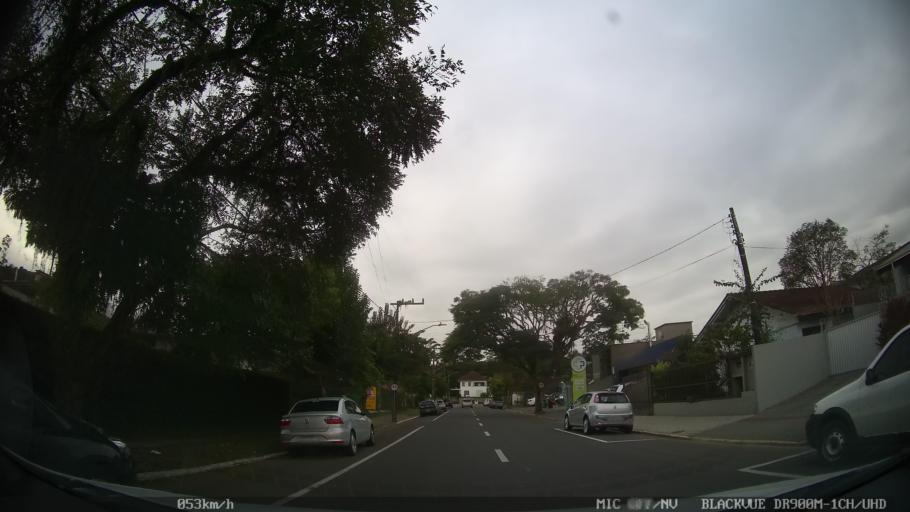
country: BR
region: Santa Catarina
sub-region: Joinville
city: Joinville
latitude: -26.2932
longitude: -48.8525
